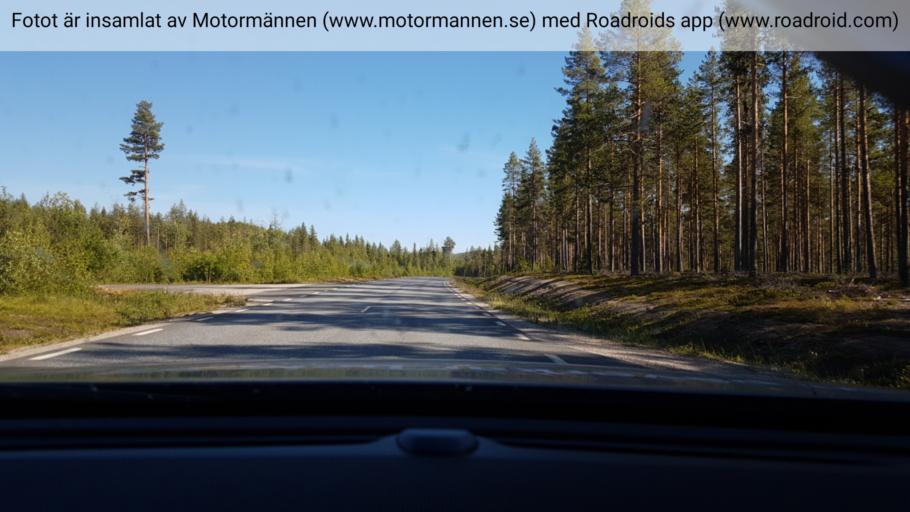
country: SE
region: Vaesterbotten
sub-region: Lycksele Kommun
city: Lycksele
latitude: 64.4117
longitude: 19.0198
